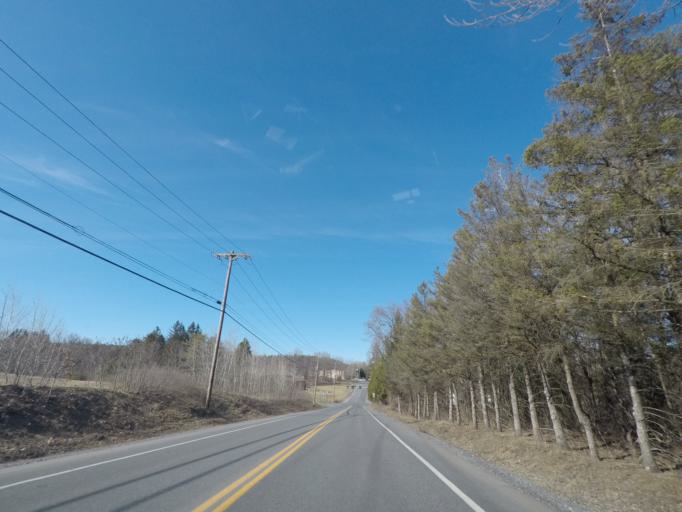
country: US
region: New York
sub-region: Saratoga County
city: Milton
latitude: 43.0742
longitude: -73.8481
